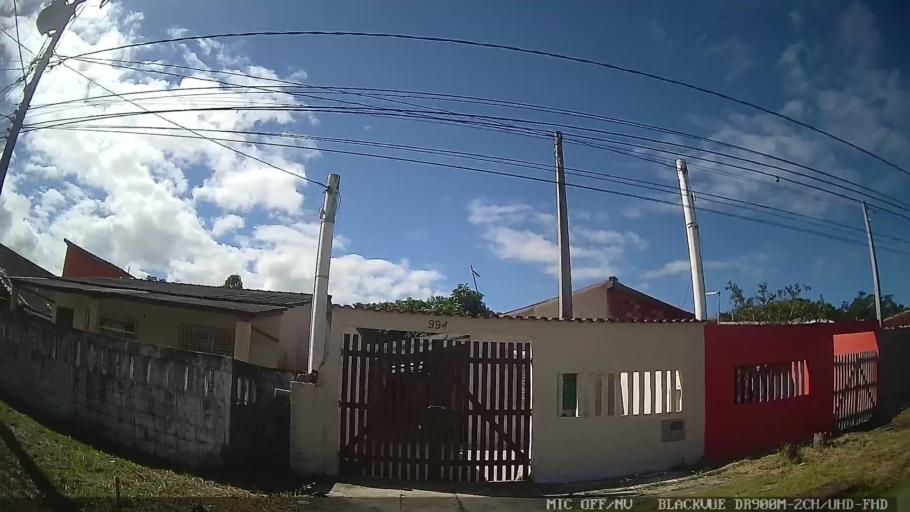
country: BR
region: Sao Paulo
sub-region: Itanhaem
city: Itanhaem
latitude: -24.2245
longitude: -46.8732
